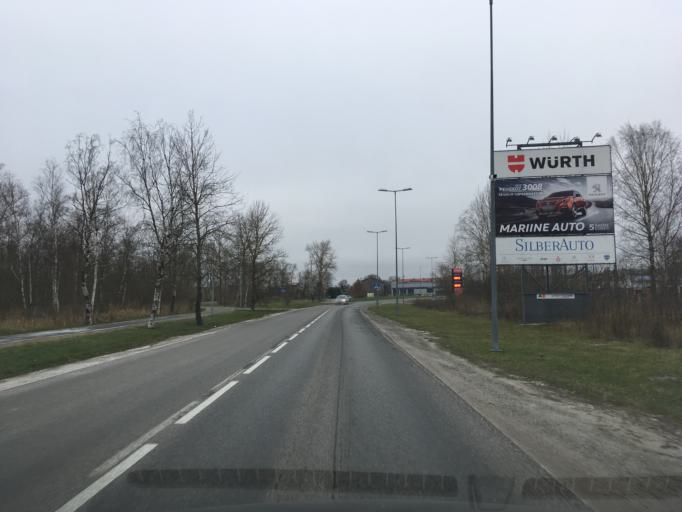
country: EE
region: Ida-Virumaa
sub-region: Johvi vald
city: Johvi
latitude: 59.3676
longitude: 27.4171
